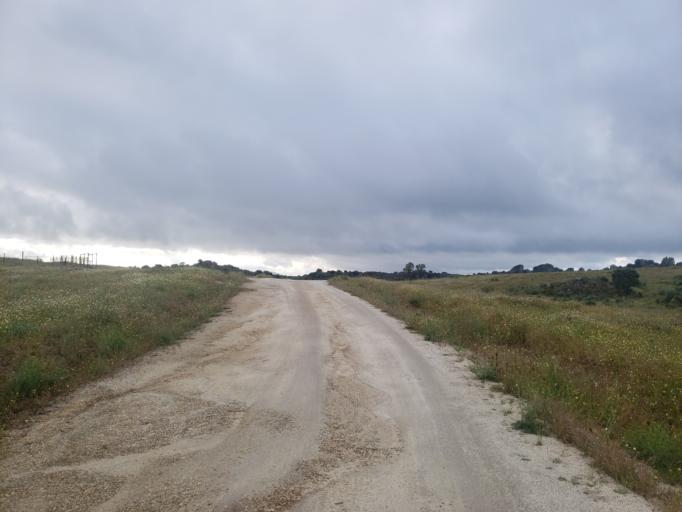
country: ES
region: Extremadura
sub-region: Provincia de Caceres
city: Malpartida de Caceres
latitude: 39.4274
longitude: -6.5029
